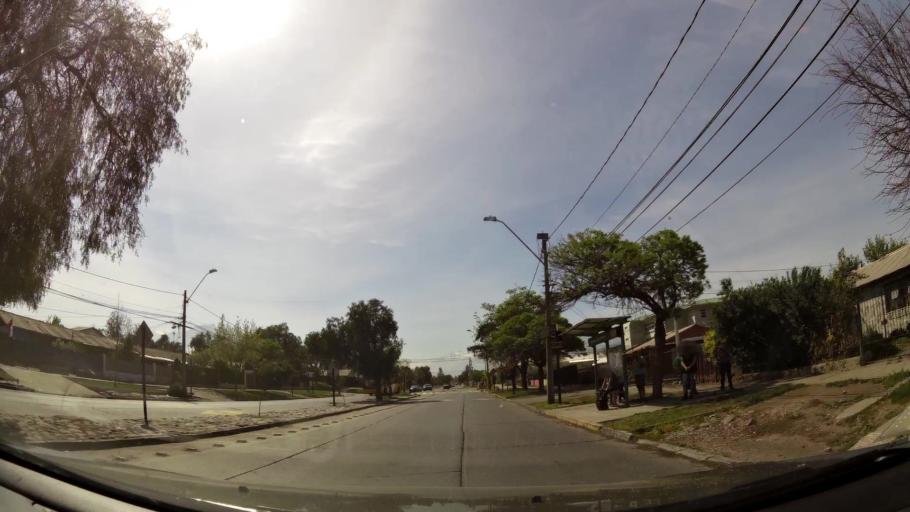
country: CL
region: Santiago Metropolitan
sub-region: Provincia de Cordillera
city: Puente Alto
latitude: -33.6184
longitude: -70.5886
